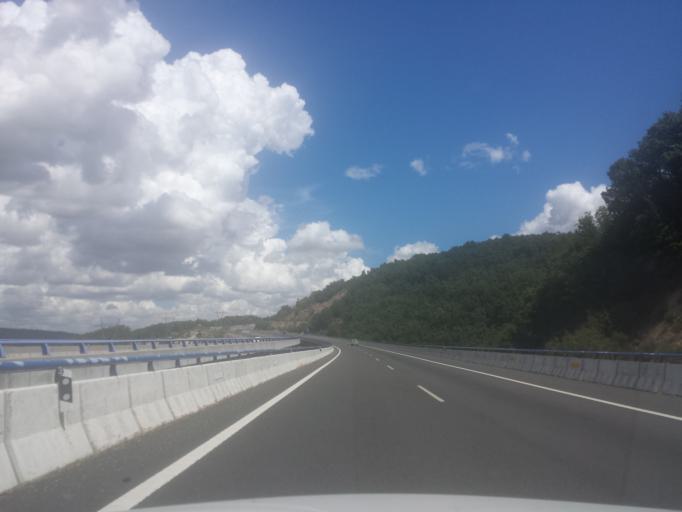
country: ES
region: Castille and Leon
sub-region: Provincia de Salamanca
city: Puerto de Bejar
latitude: 40.3574
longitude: -5.8395
